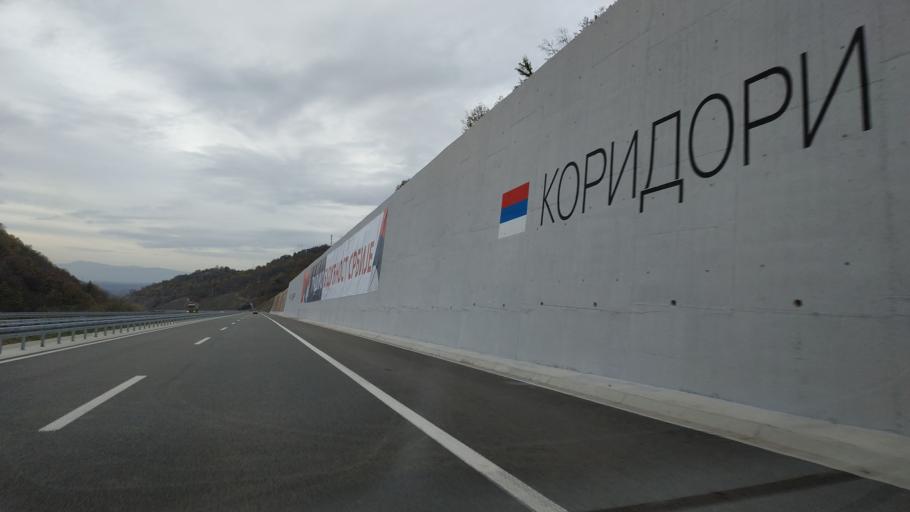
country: RS
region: Central Serbia
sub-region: Nisavski Okrug
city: Niska Banja
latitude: 43.2939
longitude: 22.0956
